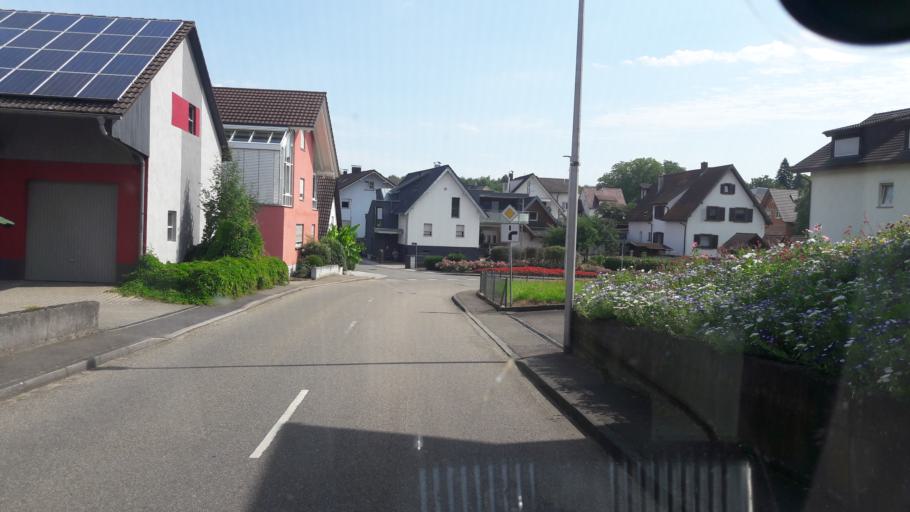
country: DE
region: Baden-Wuerttemberg
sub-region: Freiburg Region
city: Appenweier
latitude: 48.5217
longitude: 7.9995
